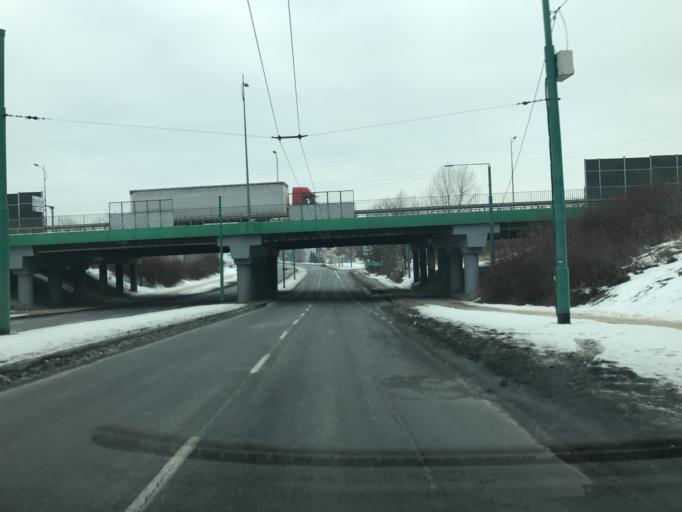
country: PL
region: Silesian Voivodeship
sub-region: Tychy
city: Cielmice
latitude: 50.1006
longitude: 19.0064
